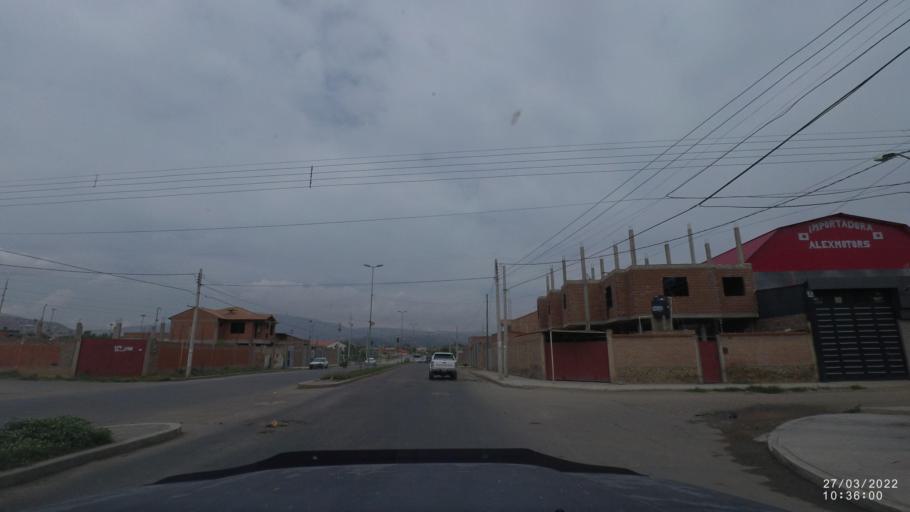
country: BO
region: Cochabamba
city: Cochabamba
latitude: -17.4413
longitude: -66.1519
